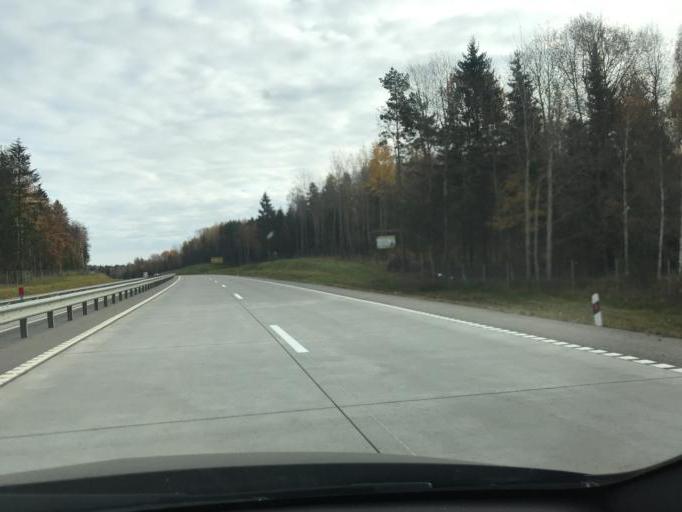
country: BY
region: Minsk
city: Syomkava
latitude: 54.0621
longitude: 27.4049
